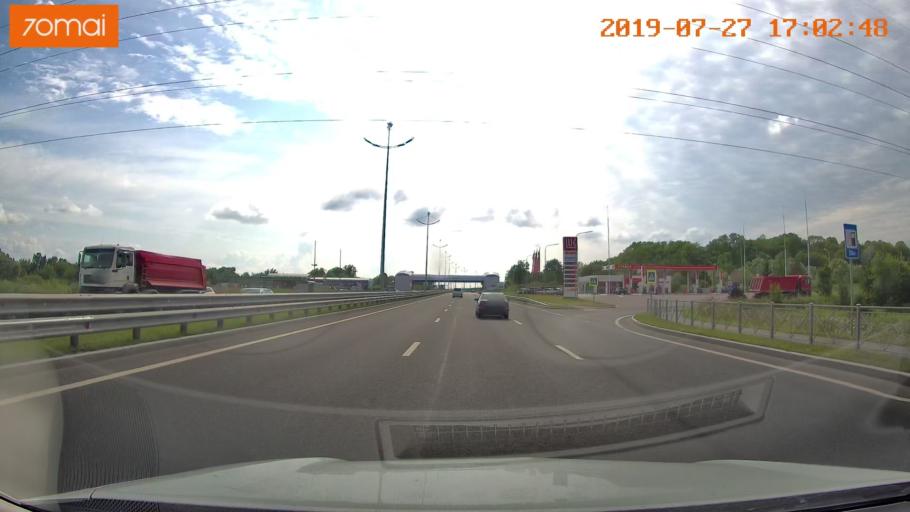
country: RU
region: Kaliningrad
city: Bol'shoe Isakovo
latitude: 54.7057
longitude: 20.6108
